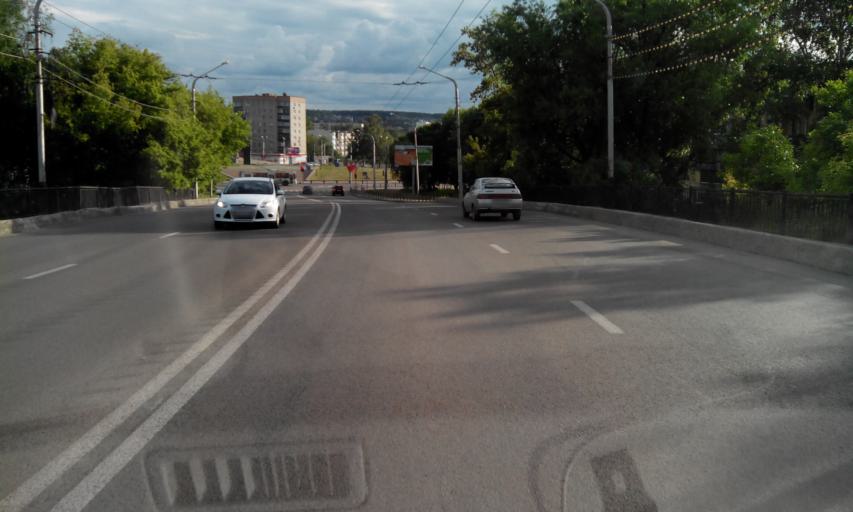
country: RU
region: Penza
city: Penza
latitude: 53.2148
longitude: 44.9907
